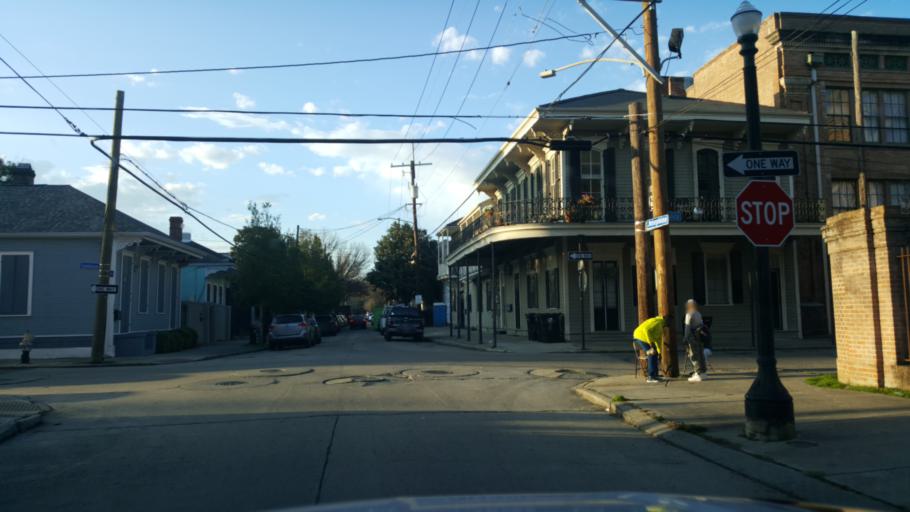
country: US
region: Louisiana
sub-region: Orleans Parish
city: New Orleans
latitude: 29.9292
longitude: -90.0749
